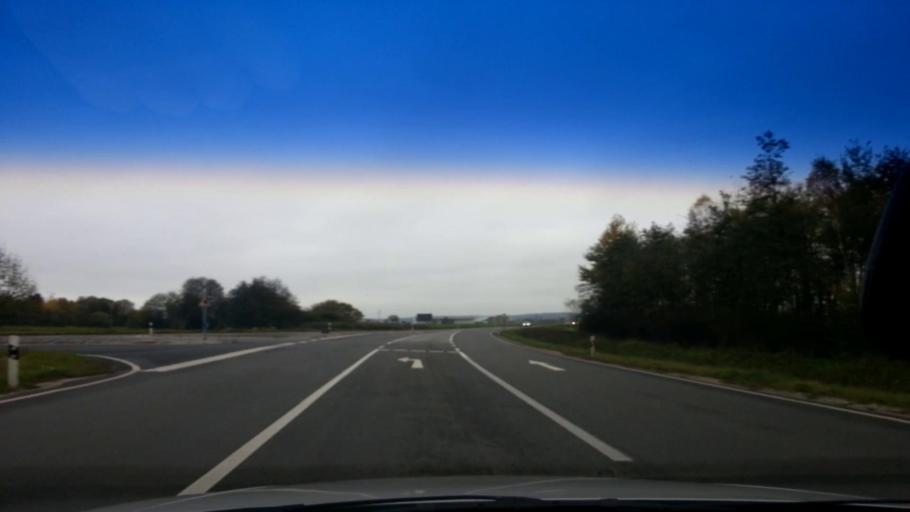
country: DE
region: Bavaria
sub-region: Upper Franconia
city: Burgebrach
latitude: 49.8274
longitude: 10.7769
